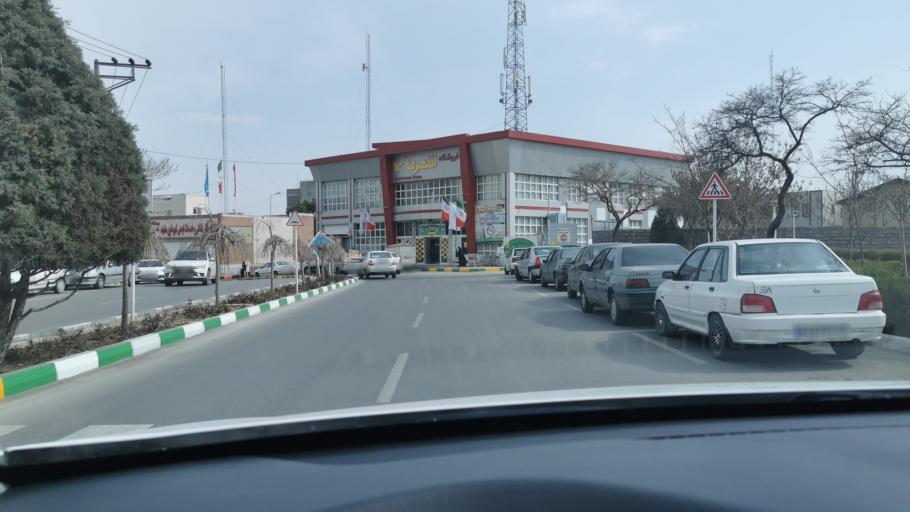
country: IR
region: Razavi Khorasan
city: Mashhad
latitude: 36.2742
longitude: 59.5678
